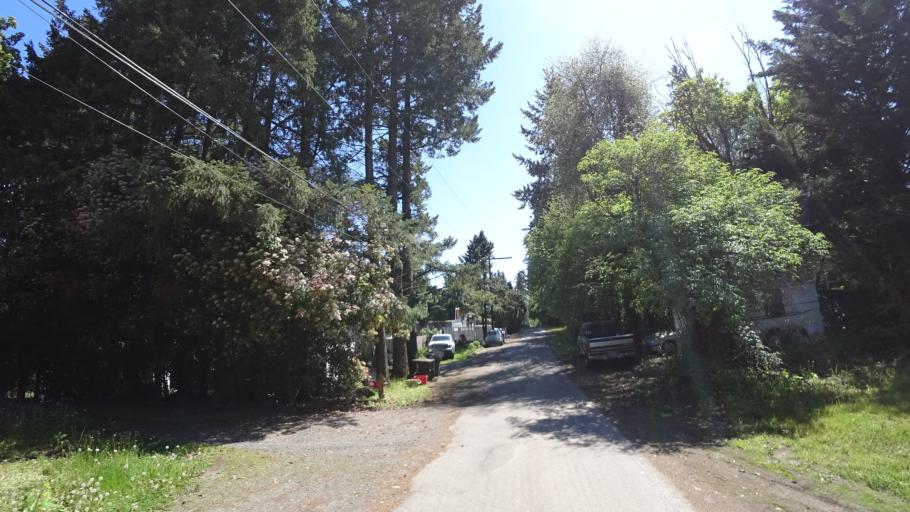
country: US
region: Oregon
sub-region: Washington County
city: Hillsboro
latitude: 45.5045
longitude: -122.9496
